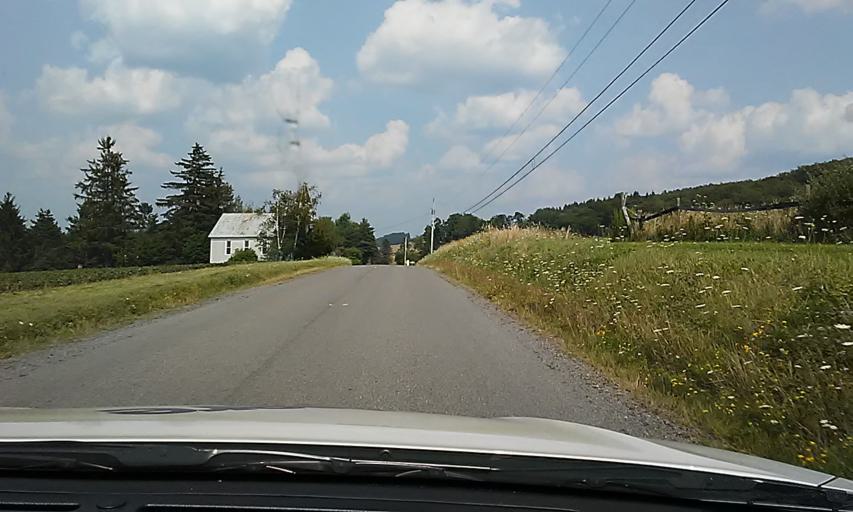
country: US
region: Pennsylvania
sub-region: Potter County
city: Coudersport
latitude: 41.8010
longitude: -77.8741
